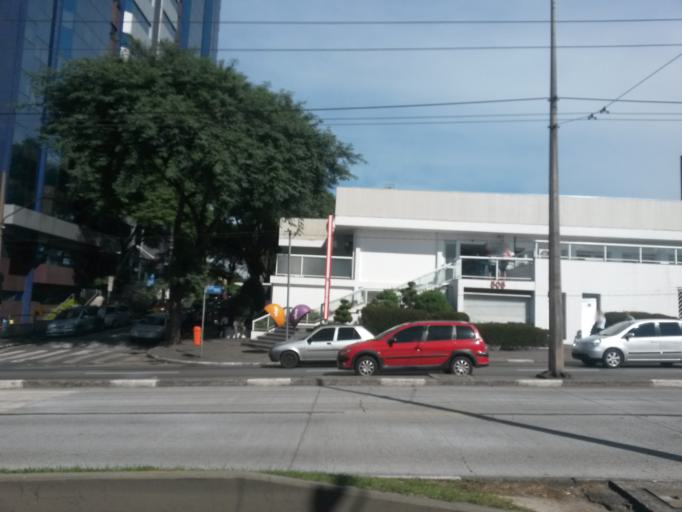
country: BR
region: Sao Paulo
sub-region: Sao Bernardo Do Campo
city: Sao Bernardo do Campo
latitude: -23.6927
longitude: -46.5549
